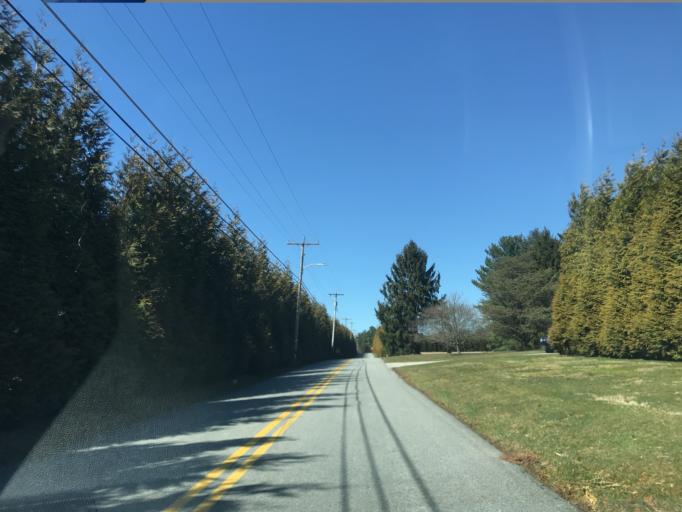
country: US
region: Pennsylvania
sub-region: York County
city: New Freedom
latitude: 39.6864
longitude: -76.6866
